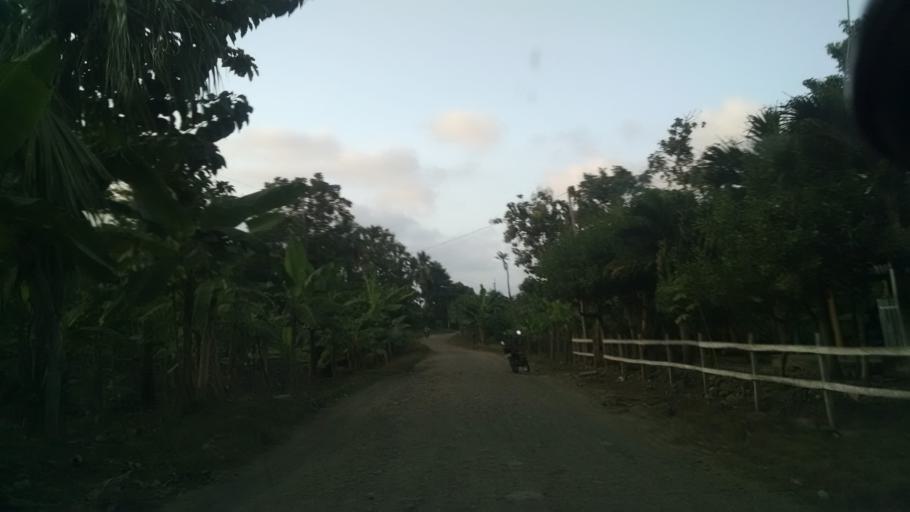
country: CO
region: Antioquia
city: San Juan de Uraba
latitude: 8.7246
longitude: -76.6044
